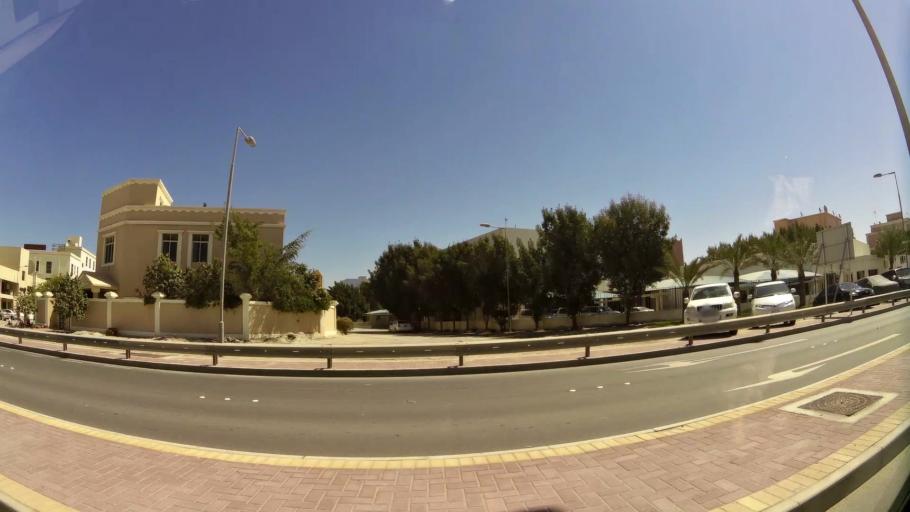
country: BH
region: Muharraq
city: Al Muharraq
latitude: 26.2710
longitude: 50.6040
